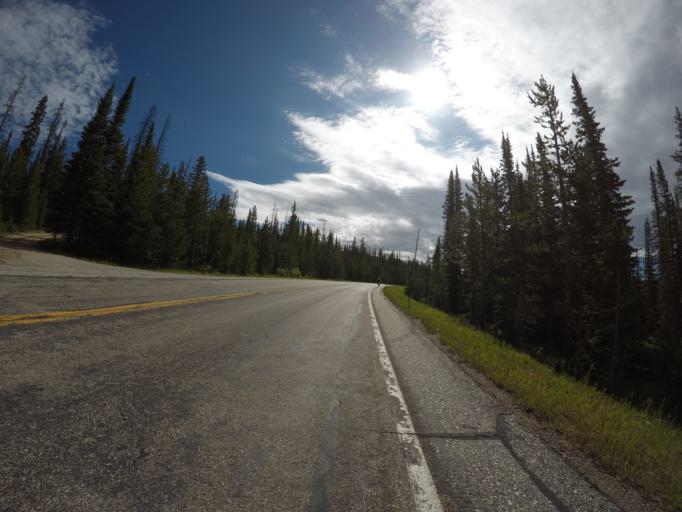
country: US
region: Wyoming
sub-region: Carbon County
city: Saratoga
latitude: 41.3263
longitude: -106.4328
